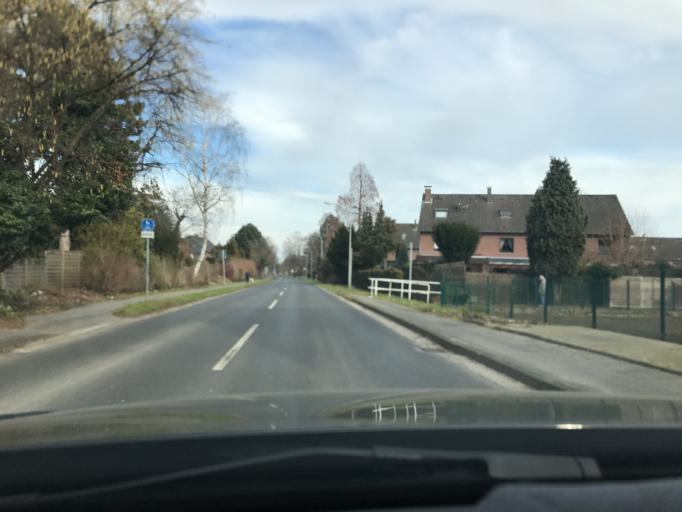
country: DE
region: North Rhine-Westphalia
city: Tonisvorst
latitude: 51.3679
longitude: 6.5182
